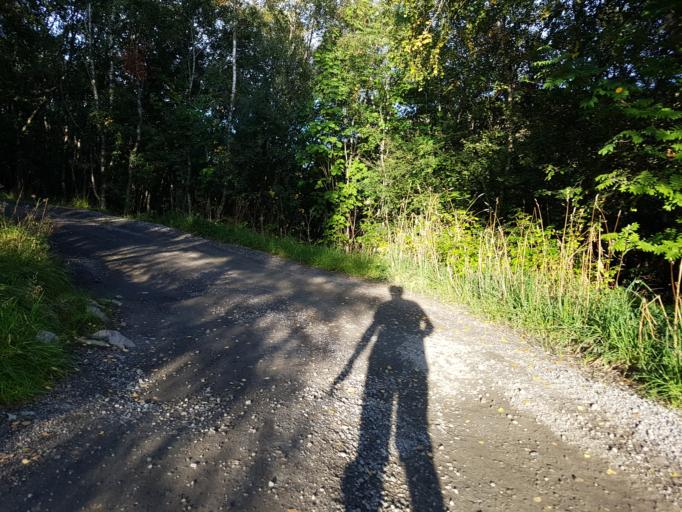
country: NO
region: Sor-Trondelag
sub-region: Afjord
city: A i Afjord
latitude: 64.0552
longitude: 9.9537
